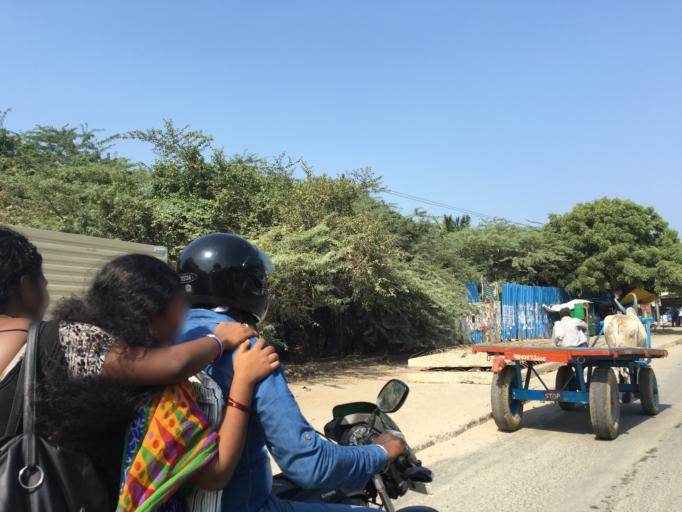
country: IN
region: Tamil Nadu
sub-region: Kancheepuram
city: Perungudi
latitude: 12.9819
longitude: 80.2330
